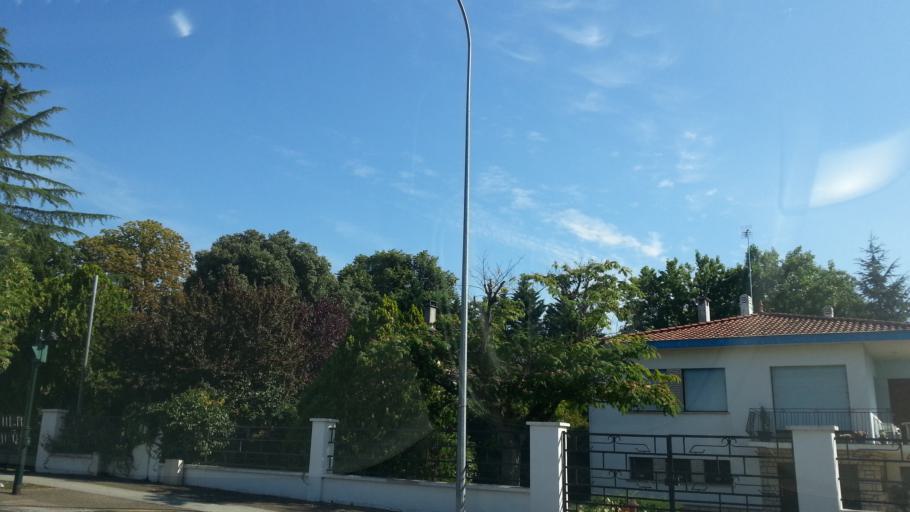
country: FR
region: Aquitaine
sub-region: Departement de la Gironde
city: Villenave-d'Ornon
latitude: 44.7636
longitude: -0.5604
